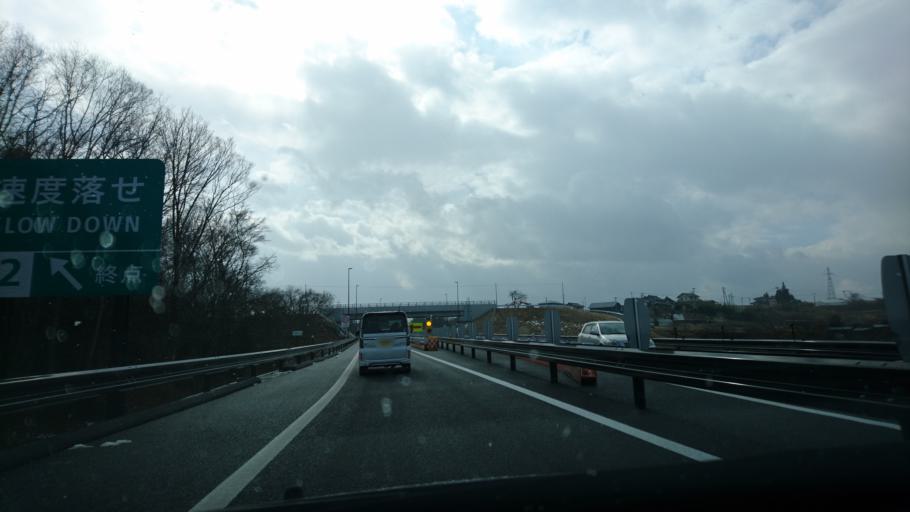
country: JP
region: Iwate
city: Ofunato
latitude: 38.7937
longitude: 141.5233
